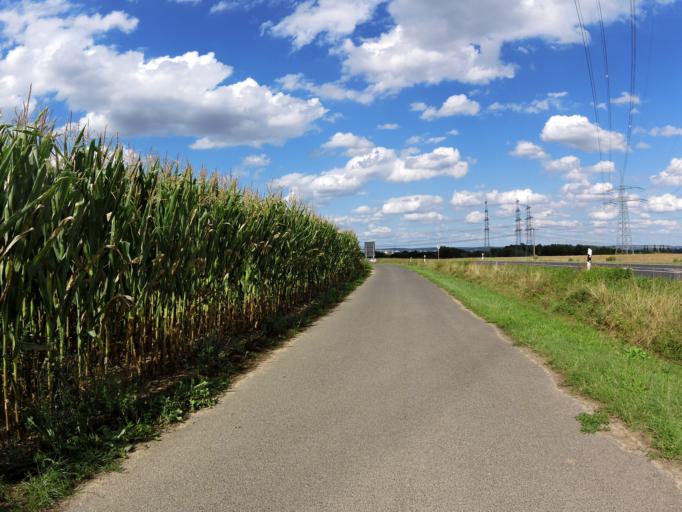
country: DE
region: Bavaria
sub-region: Regierungsbezirk Unterfranken
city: Bergrheinfeld
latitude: 49.9805
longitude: 10.1690
